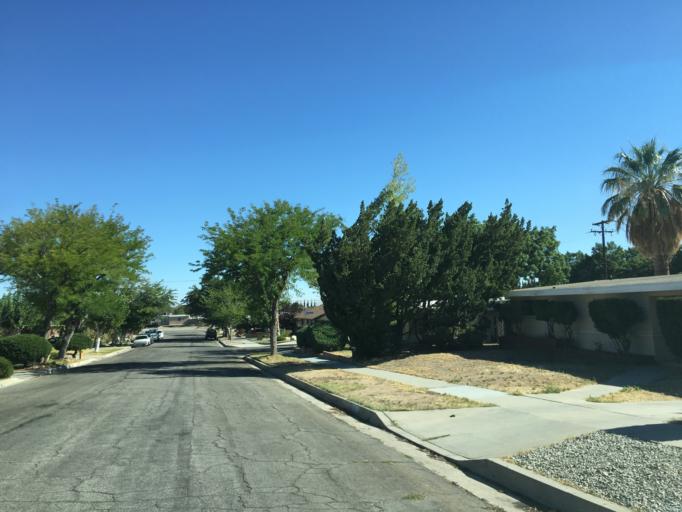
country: US
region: California
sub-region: Los Angeles County
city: Desert View Highlands
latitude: 34.5856
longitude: -118.1524
